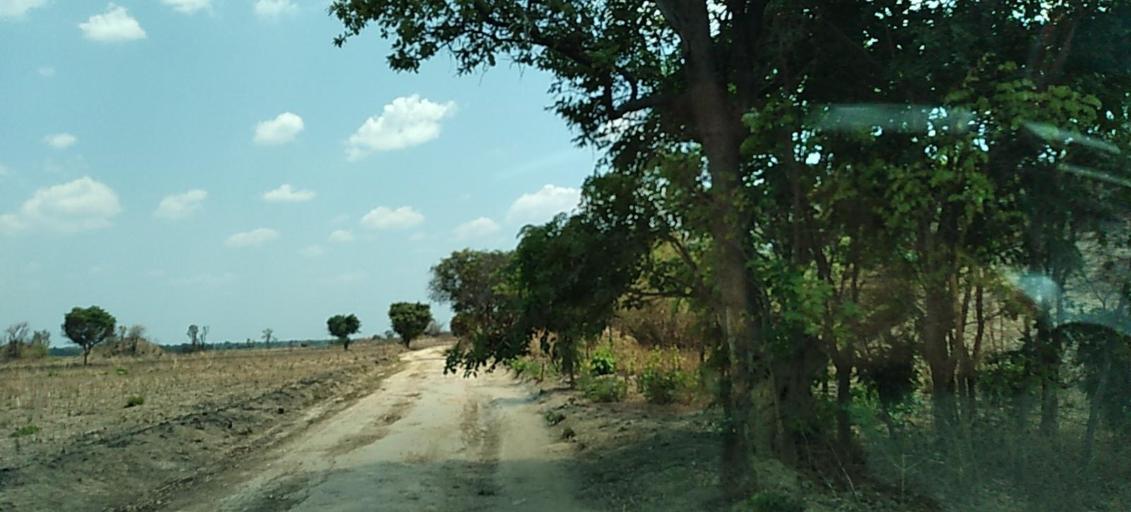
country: ZM
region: Copperbelt
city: Chililabombwe
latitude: -12.4935
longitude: 27.6659
